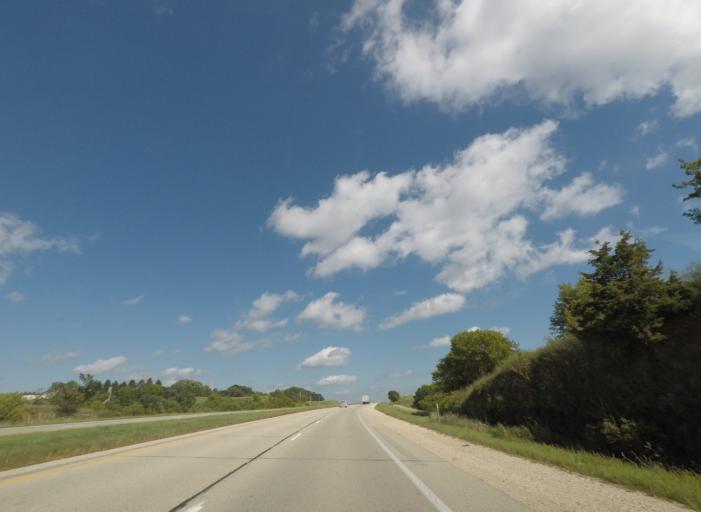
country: US
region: Iowa
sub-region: Dubuque County
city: Cascade
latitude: 42.3160
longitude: -90.9643
